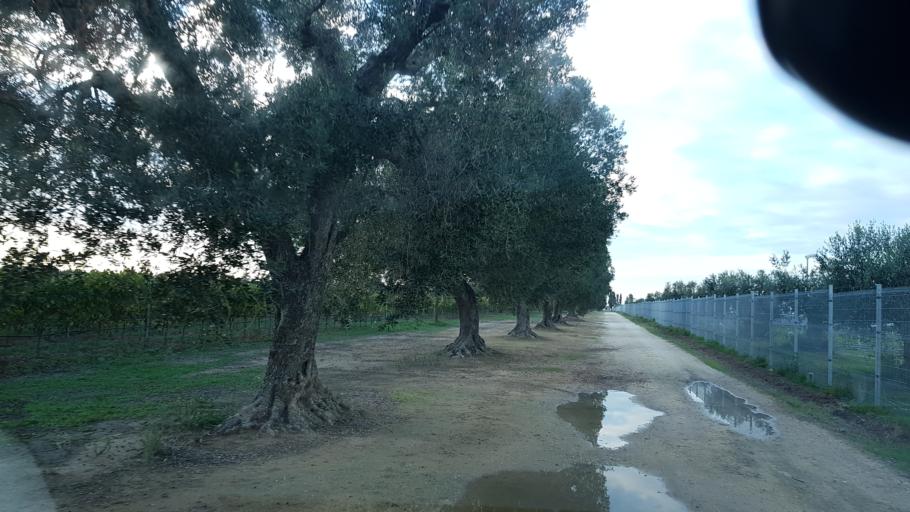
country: IT
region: Apulia
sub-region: Provincia di Brindisi
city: La Rosa
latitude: 40.5914
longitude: 17.9871
